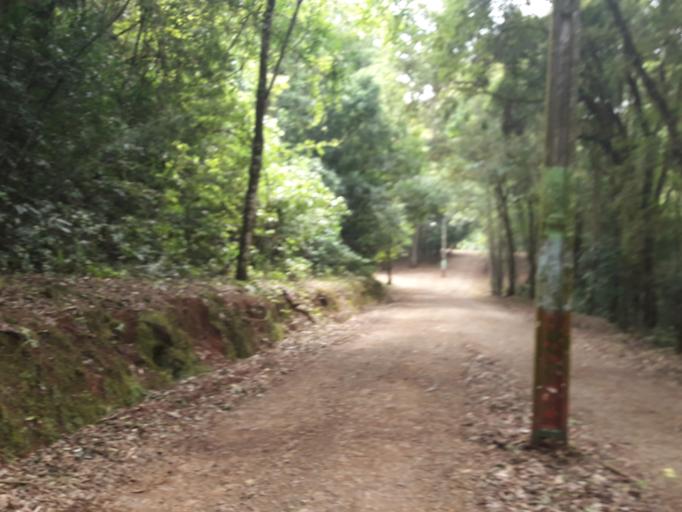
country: BR
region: Rio Grande do Sul
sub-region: Frederico Westphalen
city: Frederico Westphalen
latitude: -27.0891
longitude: -53.3787
